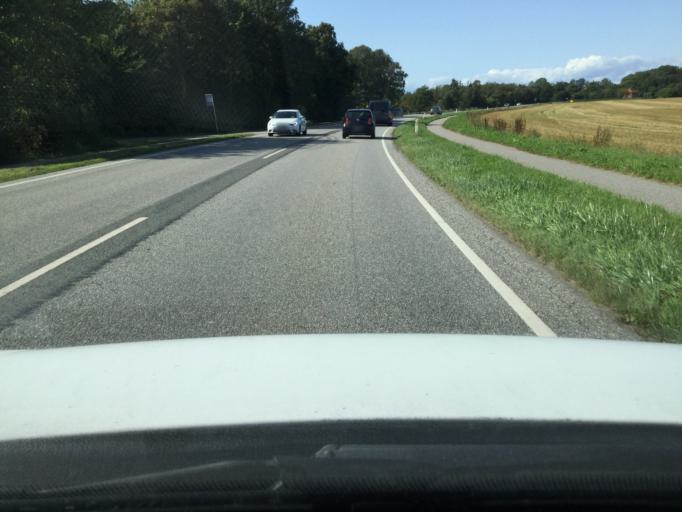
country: DK
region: Zealand
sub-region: Lolland Kommune
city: Nakskov
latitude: 54.8142
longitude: 11.1623
